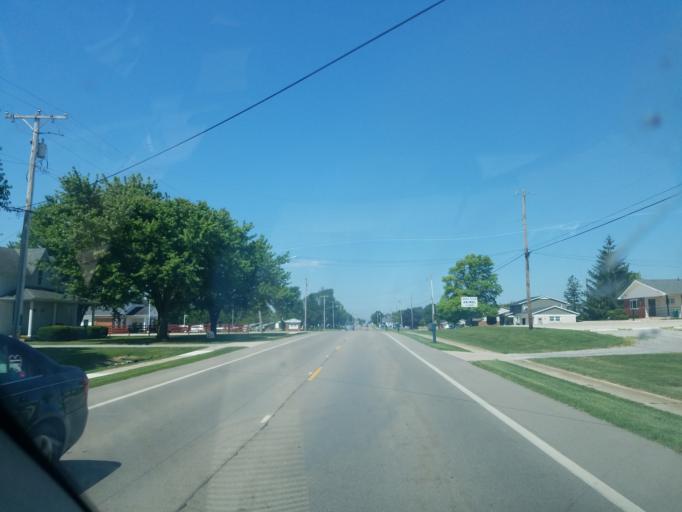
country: US
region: Ohio
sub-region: Auglaize County
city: New Bremen
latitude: 40.4077
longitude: -84.4868
